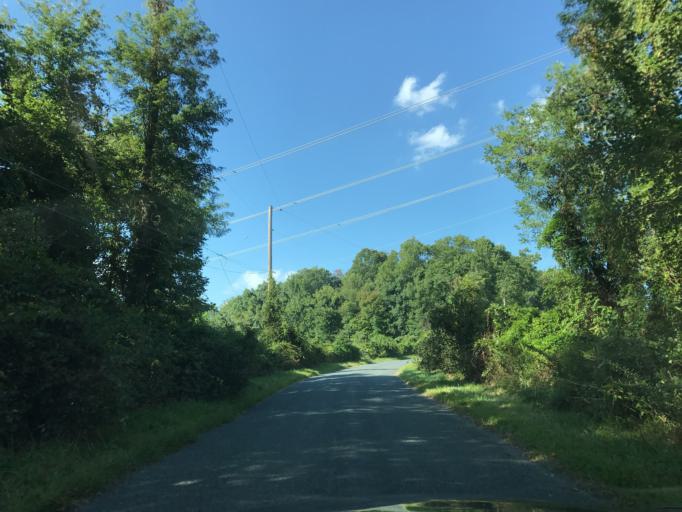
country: US
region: Pennsylvania
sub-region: York County
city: Stewartstown
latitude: 39.6996
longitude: -76.5582
